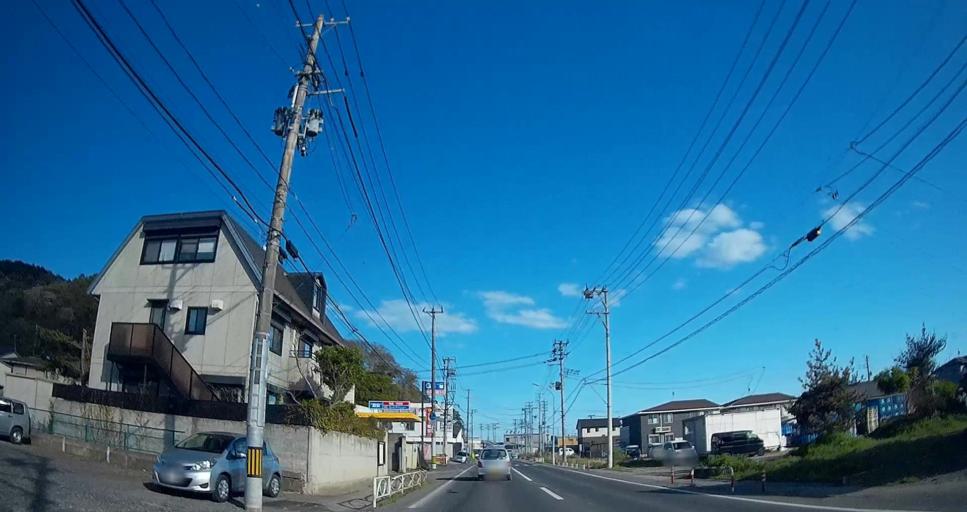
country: JP
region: Miyagi
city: Ishinomaki
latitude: 38.4224
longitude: 141.3204
